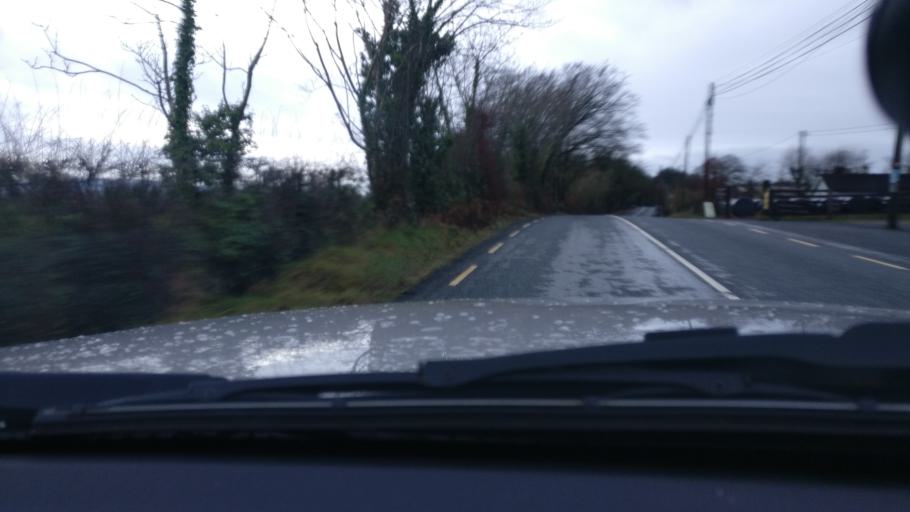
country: IE
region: Ulster
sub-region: An Cabhan
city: Ballyjamesduff
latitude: 53.8481
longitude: -7.2552
